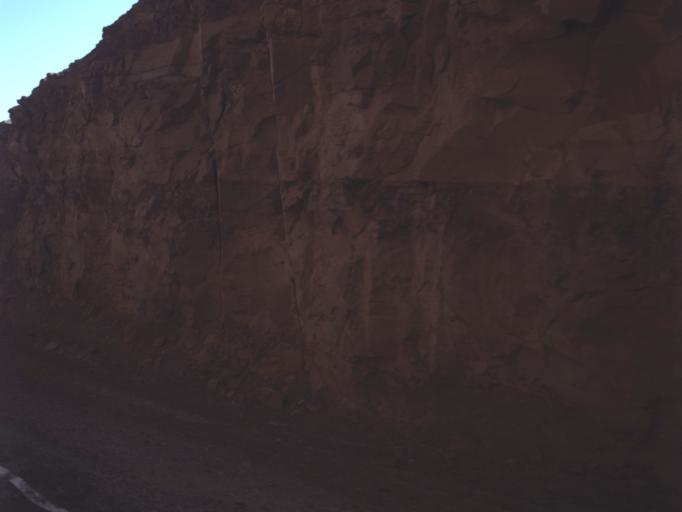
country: US
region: Utah
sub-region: San Juan County
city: Blanding
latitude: 37.8899
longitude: -110.4012
